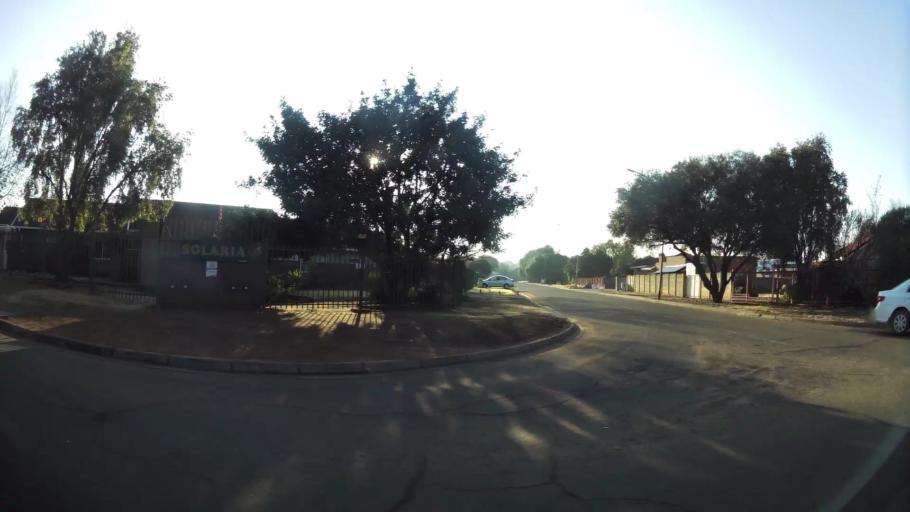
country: ZA
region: Orange Free State
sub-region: Mangaung Metropolitan Municipality
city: Bloemfontein
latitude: -29.1568
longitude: 26.1735
